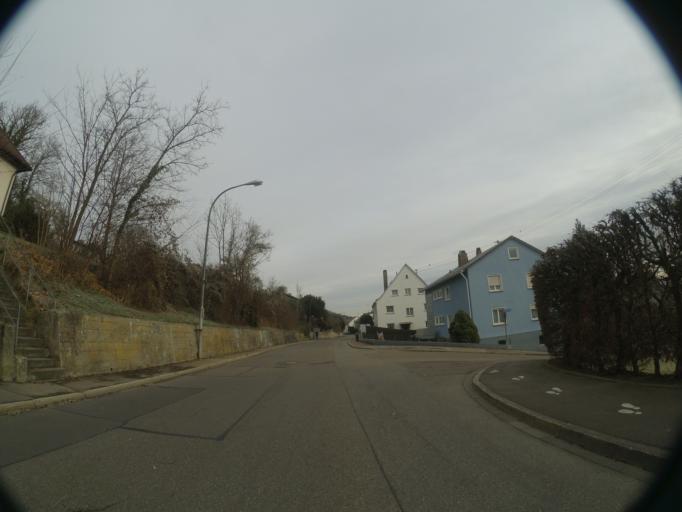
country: DE
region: Bavaria
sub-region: Swabia
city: Neu-Ulm
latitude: 48.4345
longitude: 10.0459
